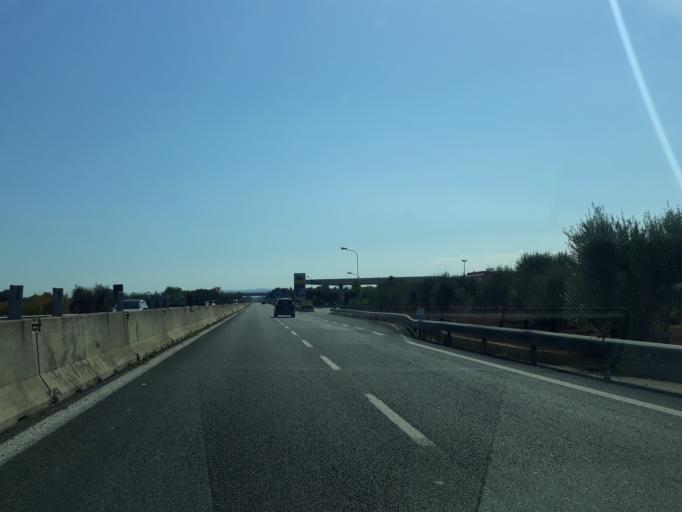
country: IT
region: Apulia
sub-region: Provincia di Bari
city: Monopoli
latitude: 40.9120
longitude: 17.3217
